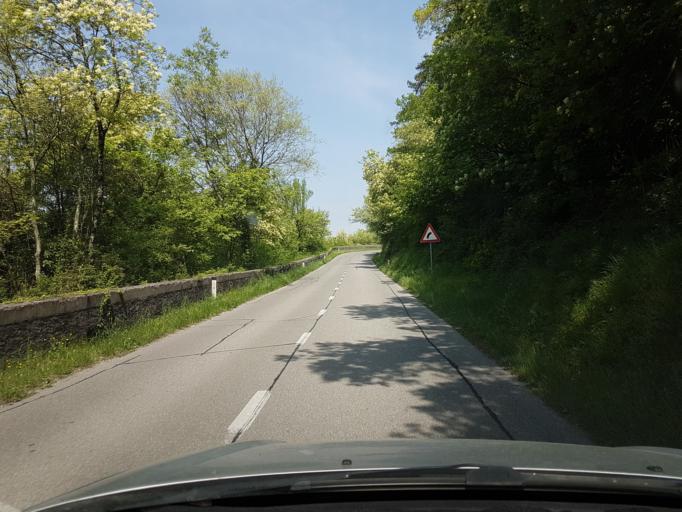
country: SI
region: Komen
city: Komen
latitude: 45.7986
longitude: 13.7106
